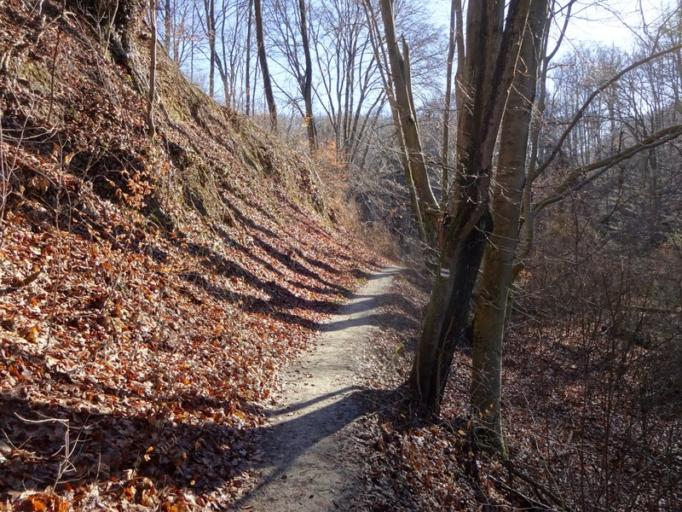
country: HU
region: Veszprem
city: Cseteny
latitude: 47.2692
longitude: 17.9884
